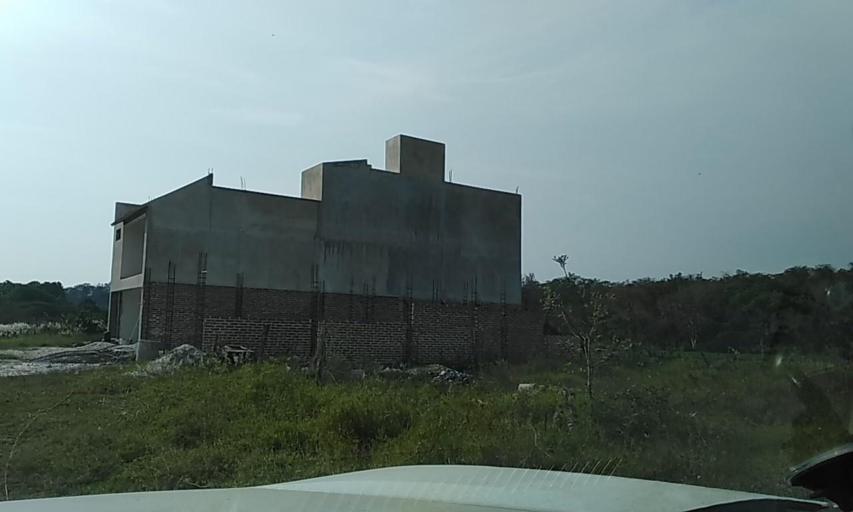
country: MX
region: Veracruz
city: El Castillo
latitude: 19.5413
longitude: -96.8475
